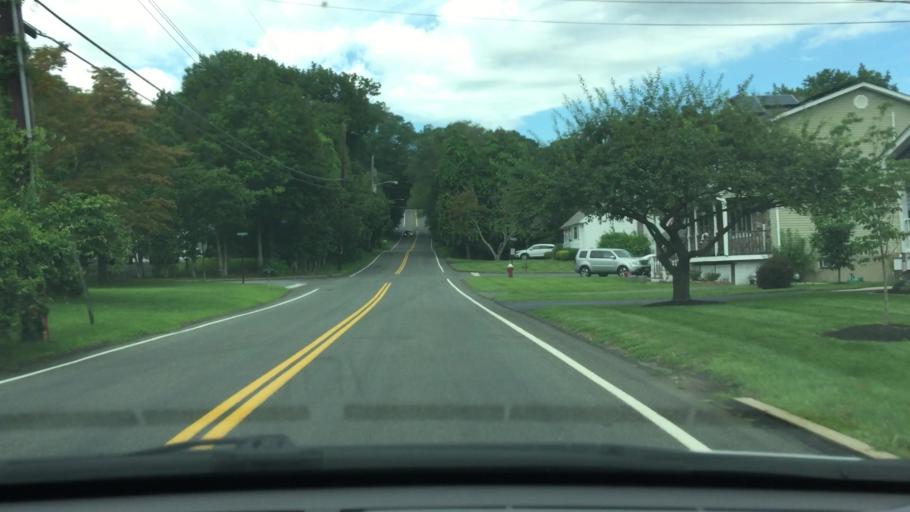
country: US
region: New York
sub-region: Rockland County
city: Stony Point
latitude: 41.2256
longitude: -73.9997
